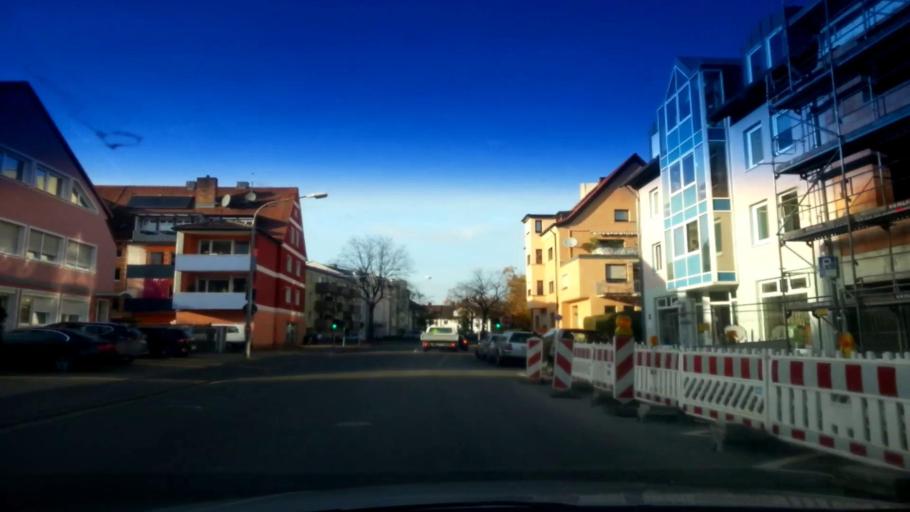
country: DE
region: Bavaria
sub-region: Upper Franconia
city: Bamberg
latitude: 49.8998
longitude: 10.9105
